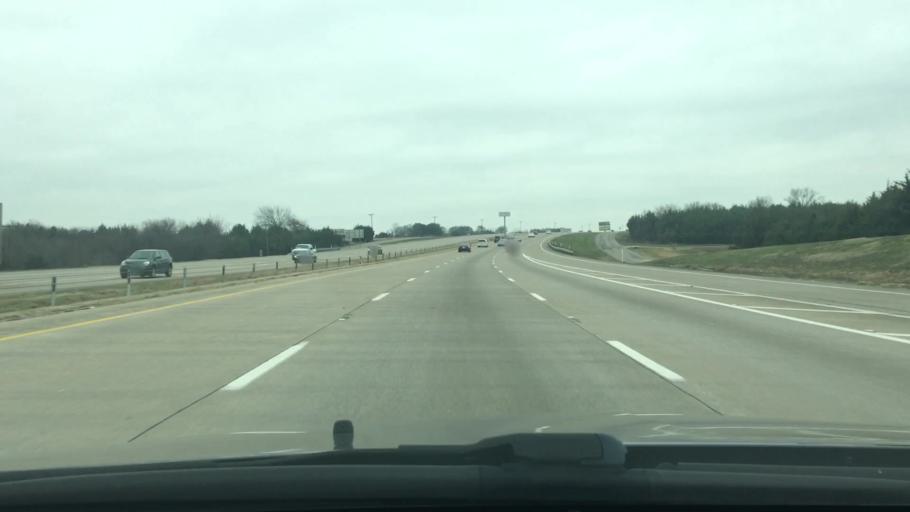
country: US
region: Texas
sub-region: Ellis County
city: Palmer
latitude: 32.4304
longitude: -96.6591
